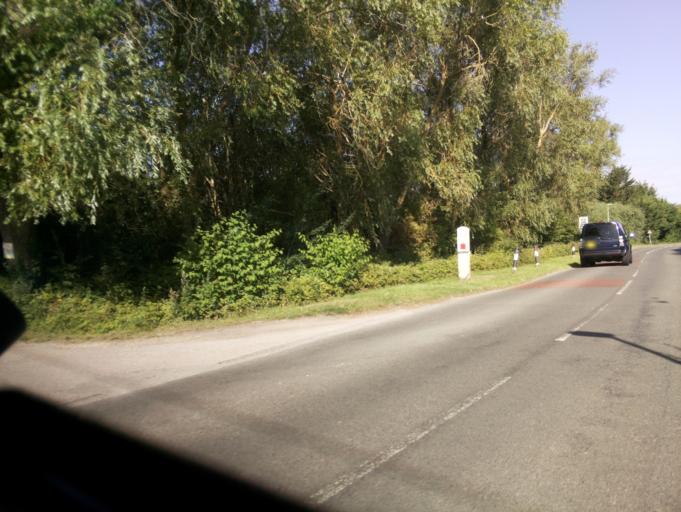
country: GB
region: England
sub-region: Oxfordshire
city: Bampton
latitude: 51.7229
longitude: -1.5366
